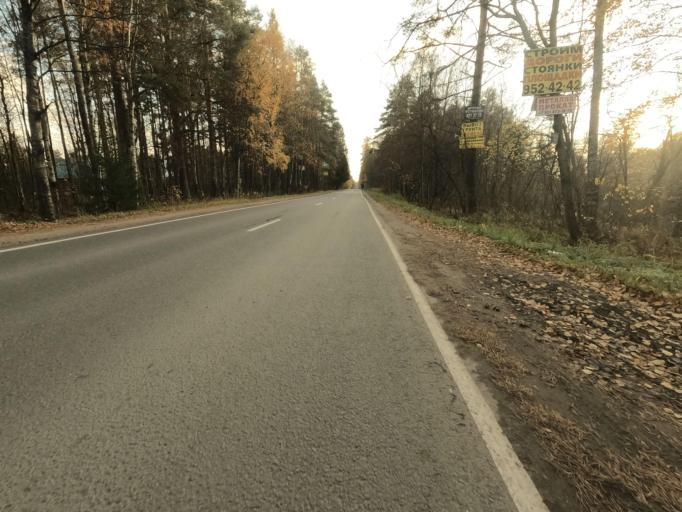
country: RU
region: St.-Petersburg
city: Beloostrov
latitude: 60.1663
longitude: 30.0100
